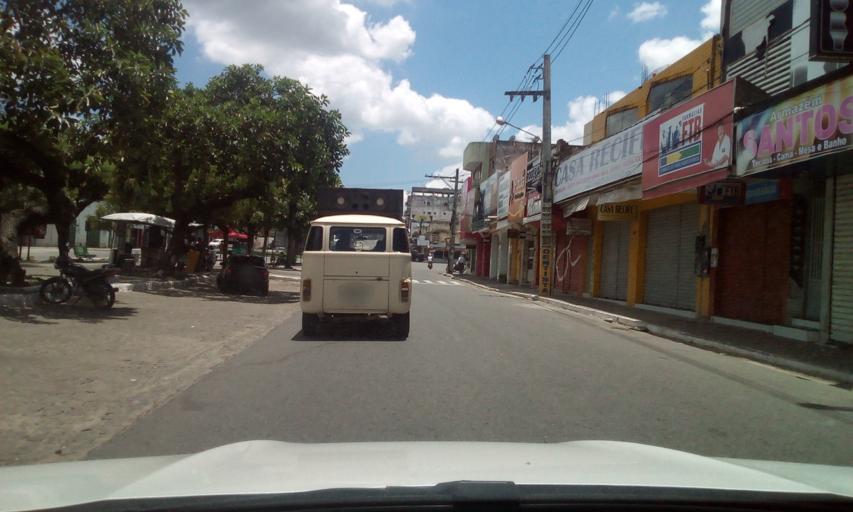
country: BR
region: Paraiba
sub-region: Guarabira
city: Guarabira
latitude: -6.8518
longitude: -35.4916
